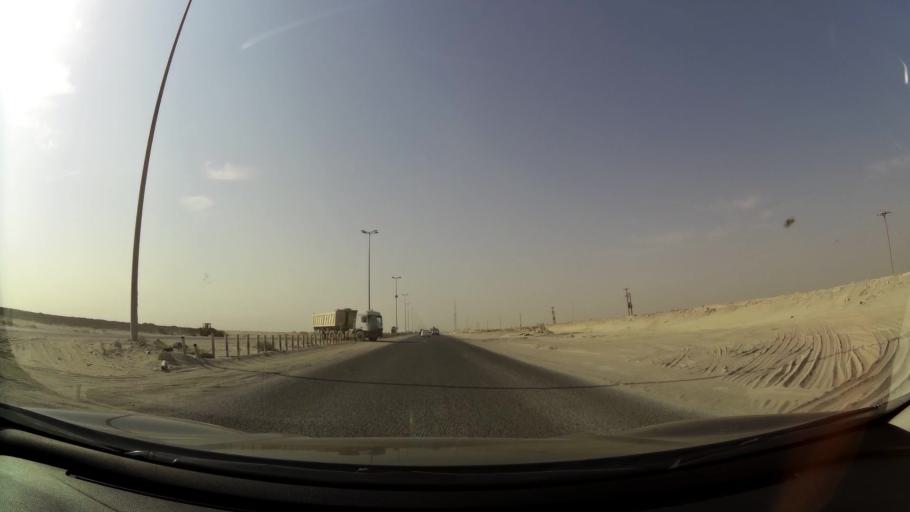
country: KW
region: Al Ahmadi
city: Al Ahmadi
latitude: 28.9133
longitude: 48.0977
